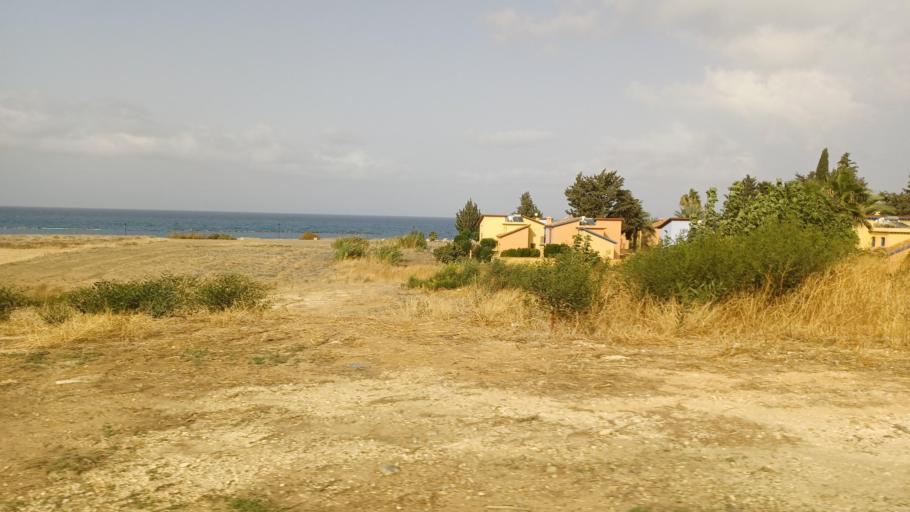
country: CY
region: Pafos
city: Polis
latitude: 35.0396
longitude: 32.4134
